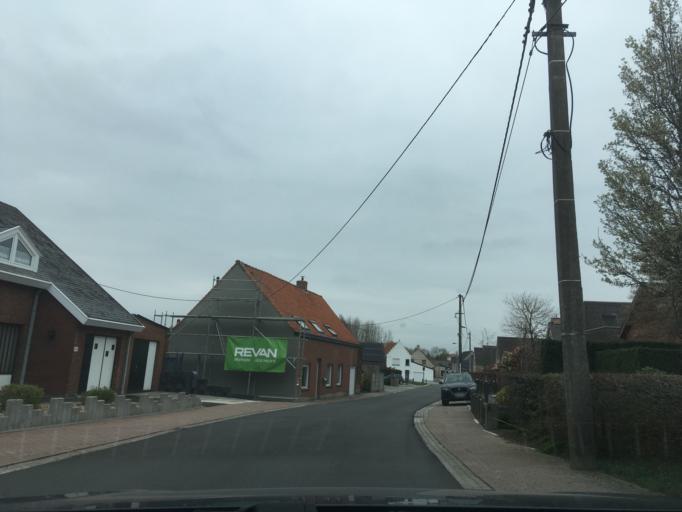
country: BE
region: Flanders
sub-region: Provincie West-Vlaanderen
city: Lichtervelde
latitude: 51.0229
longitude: 3.1454
